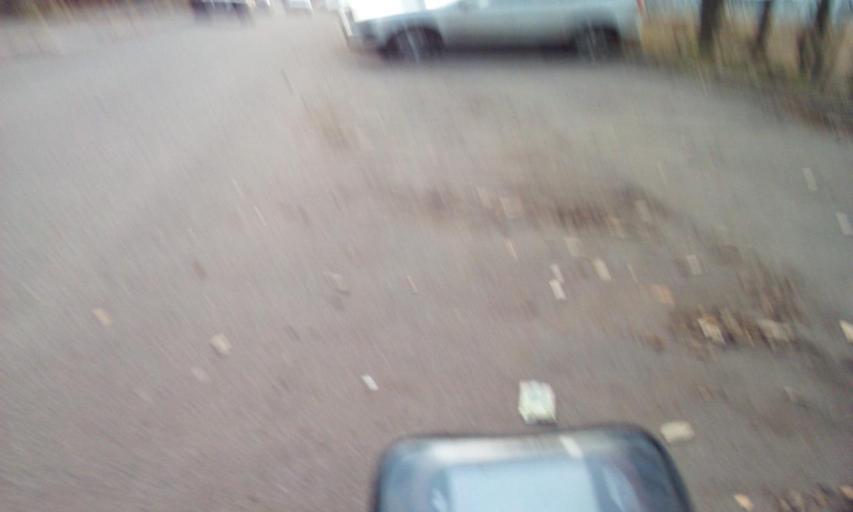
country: RU
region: Moskovskaya
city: Aprelevka
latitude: 55.5542
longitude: 37.0836
